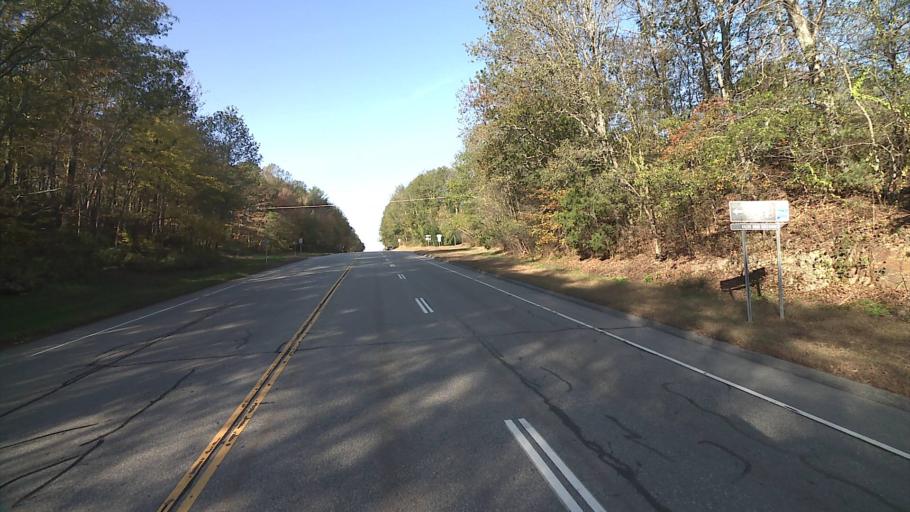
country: US
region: Connecticut
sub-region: Windham County
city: Killingly Center
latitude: 41.7908
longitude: -71.8105
